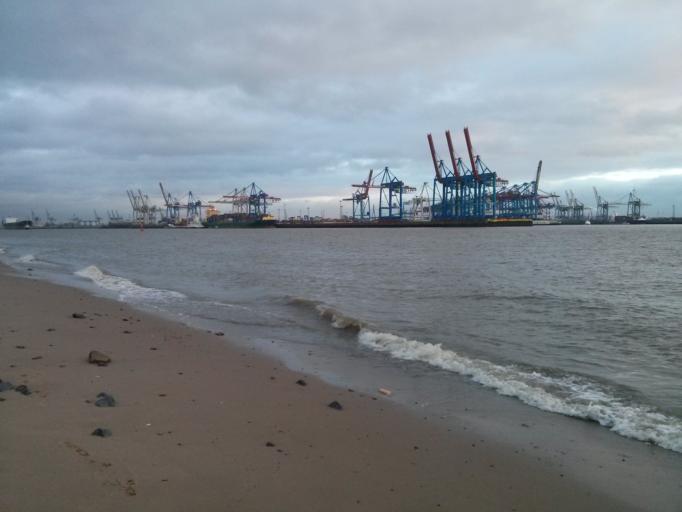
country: DE
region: Hamburg
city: Altona
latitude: 53.5443
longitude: 9.8995
